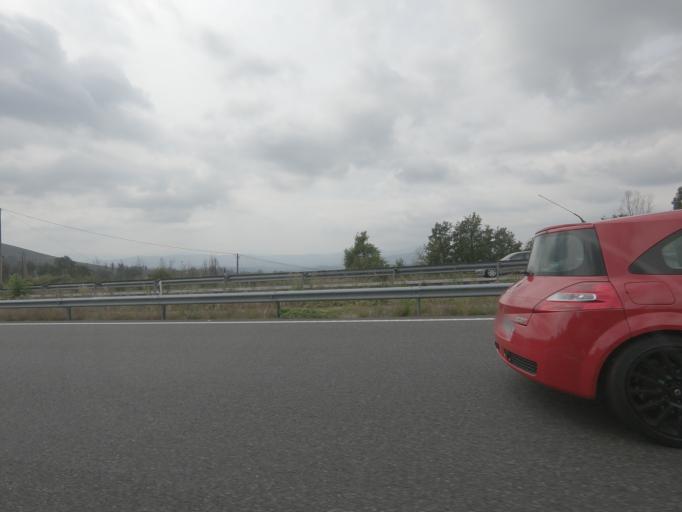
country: ES
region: Galicia
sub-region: Provincia de Pontevedra
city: Arbo
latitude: 42.1545
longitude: -8.4013
